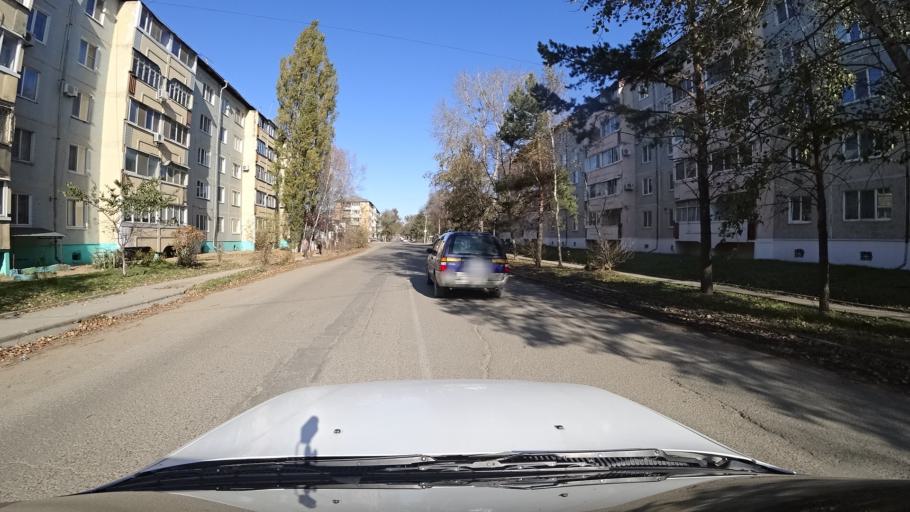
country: RU
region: Primorskiy
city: Dal'nerechensk
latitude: 45.9352
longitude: 133.7338
